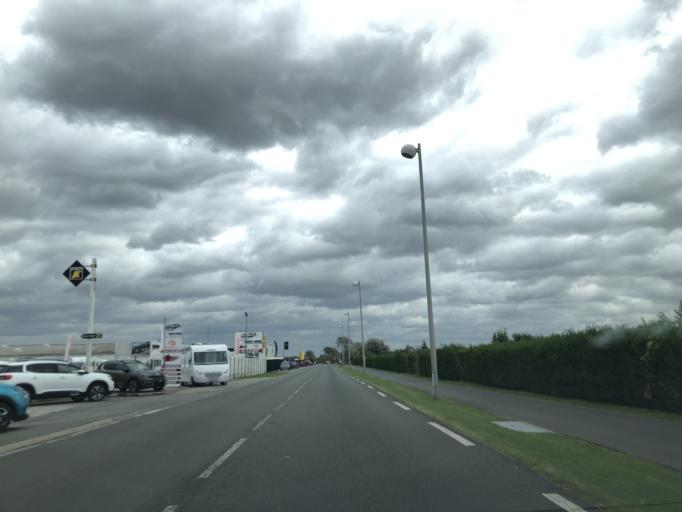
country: FR
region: Nord-Pas-de-Calais
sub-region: Departement du Pas-de-Calais
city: Berck
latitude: 50.4007
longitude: 1.5978
